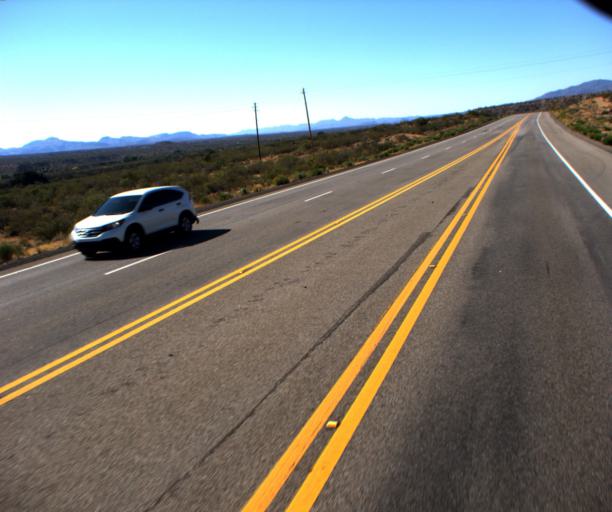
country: US
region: Arizona
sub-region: Yavapai County
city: Bagdad
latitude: 34.8119
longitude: -113.6261
